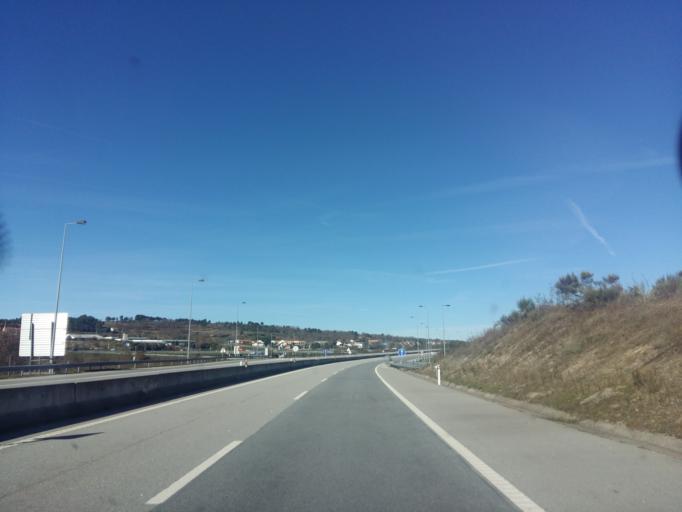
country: PT
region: Guarda
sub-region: Guarda
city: Sequeira
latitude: 40.5616
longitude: -7.2175
